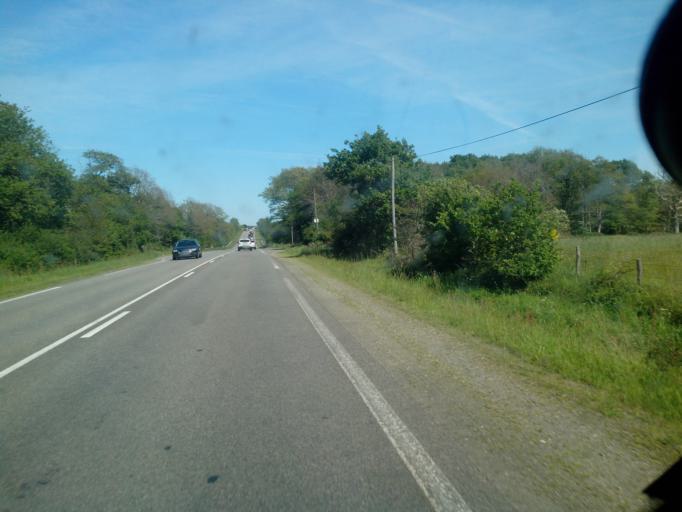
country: FR
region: Pays de la Loire
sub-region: Departement de la Loire-Atlantique
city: Chauve
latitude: 47.1114
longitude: -1.9889
